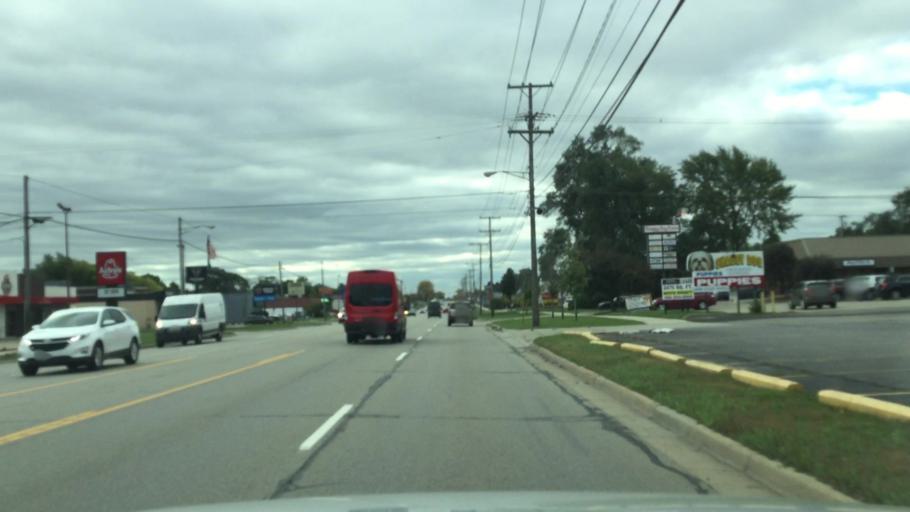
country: US
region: Michigan
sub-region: Macomb County
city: Utica
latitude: 42.6454
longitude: -83.0331
